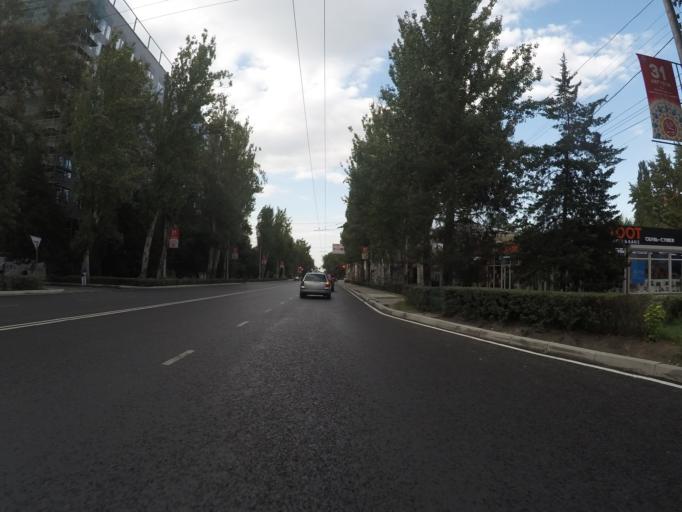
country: KG
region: Chuy
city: Bishkek
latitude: 42.8687
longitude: 74.5876
